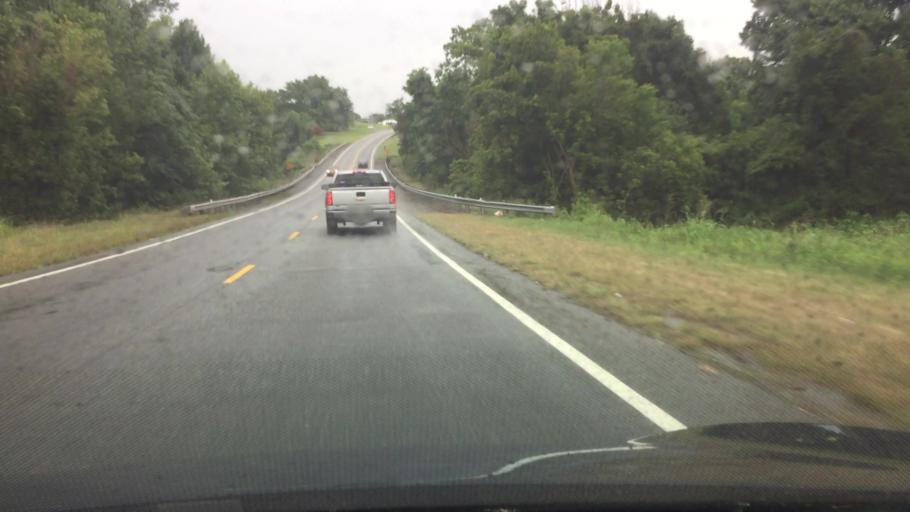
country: US
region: Virginia
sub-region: Bedford County
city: Forest
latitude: 37.3699
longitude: -79.3870
